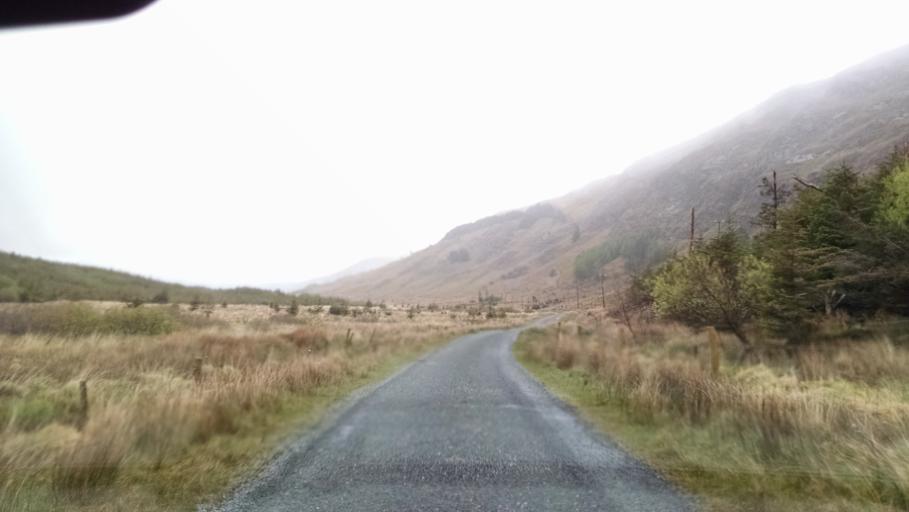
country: IE
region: Connaught
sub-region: Maigh Eo
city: Westport
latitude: 53.6449
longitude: -9.7029
